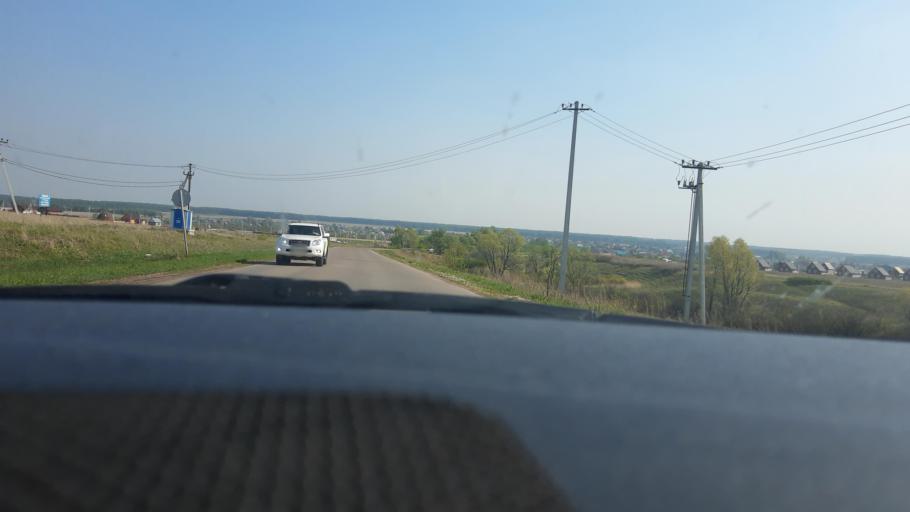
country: RU
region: Bashkortostan
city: Avdon
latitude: 54.5619
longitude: 55.7619
